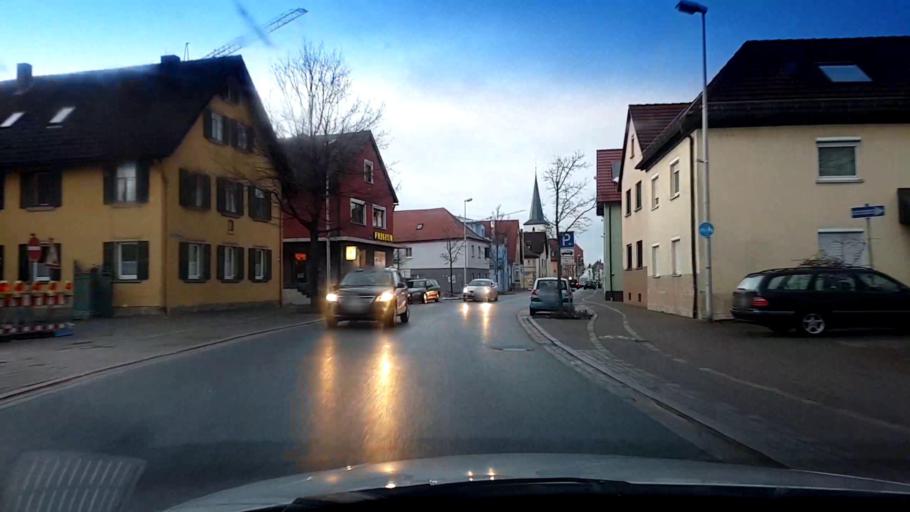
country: DE
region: Bavaria
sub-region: Upper Franconia
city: Hirschaid
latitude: 49.8145
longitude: 10.9917
